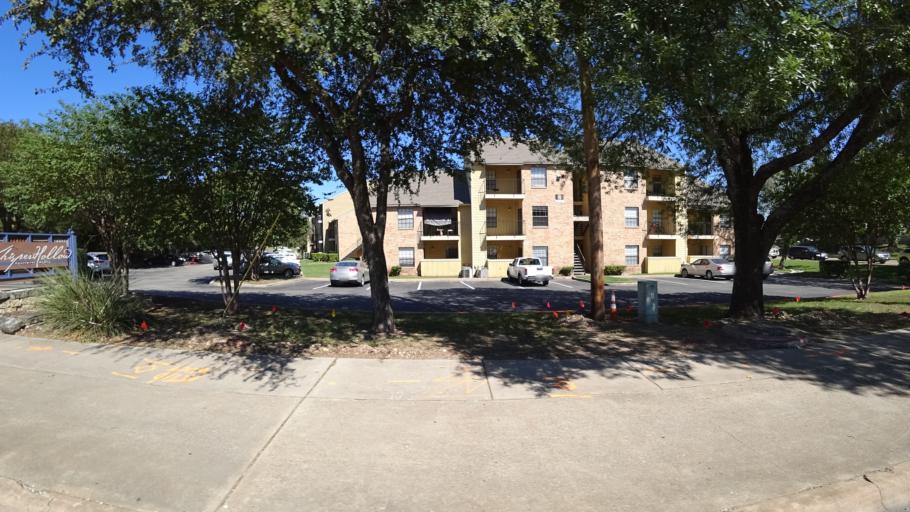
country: US
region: Texas
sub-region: Travis County
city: Austin
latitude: 30.2216
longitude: -97.7456
